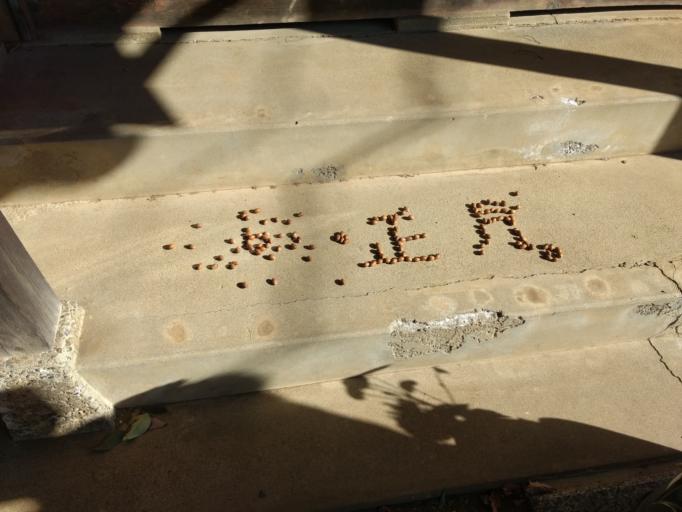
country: JP
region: Saitama
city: Shimotoda
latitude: 35.8471
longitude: 139.6594
